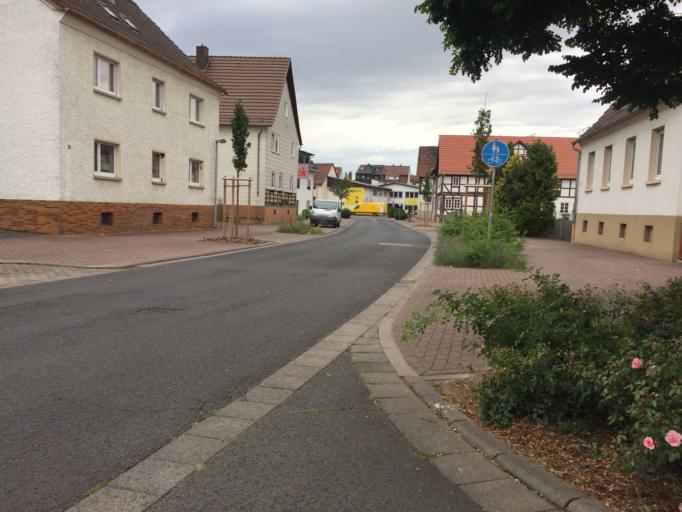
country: DE
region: Hesse
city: Bebra
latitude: 50.9716
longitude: 9.7893
